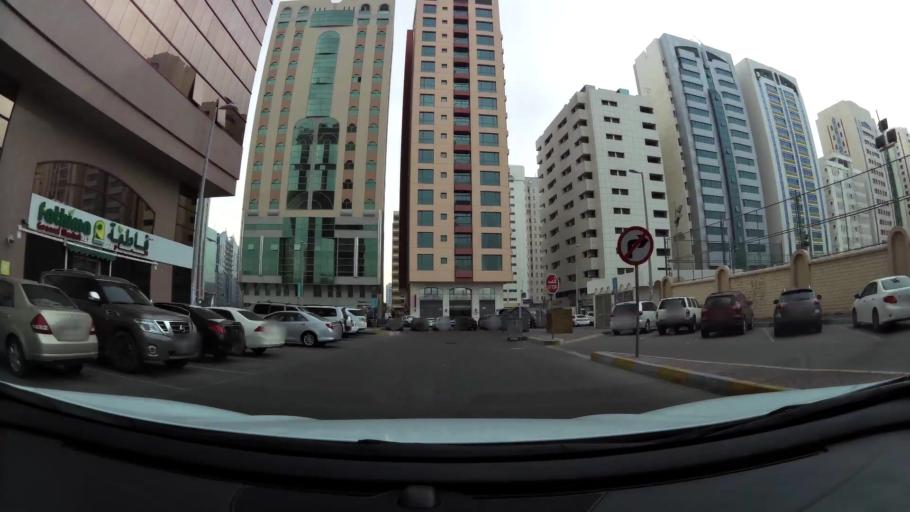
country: AE
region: Abu Dhabi
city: Abu Dhabi
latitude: 24.4797
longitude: 54.3686
